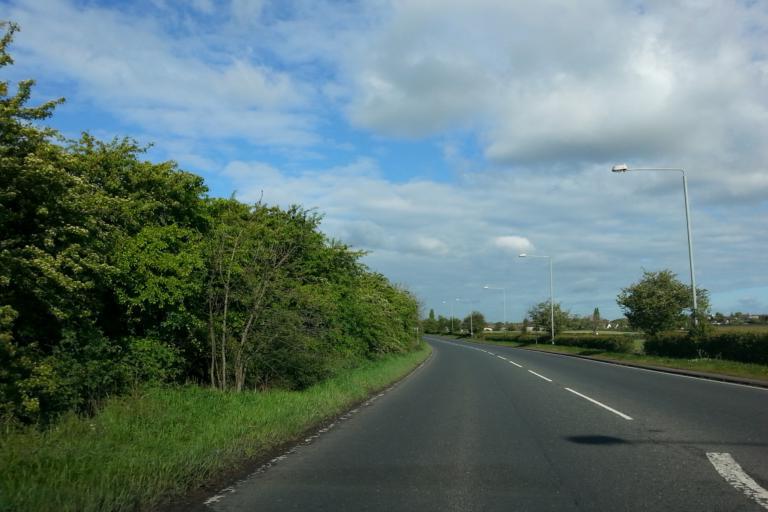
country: GB
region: England
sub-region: Nottinghamshire
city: Cotgrave
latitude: 52.8940
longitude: -1.0864
